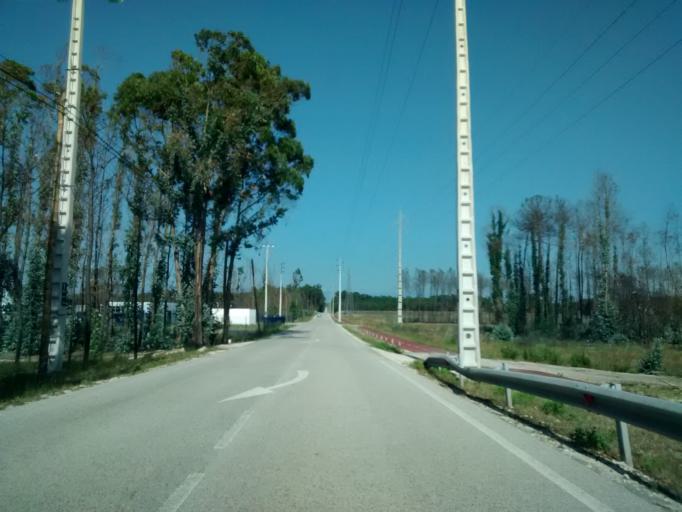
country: PT
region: Leiria
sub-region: Leiria
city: Monte Redondo
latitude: 39.9797
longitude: -8.8475
